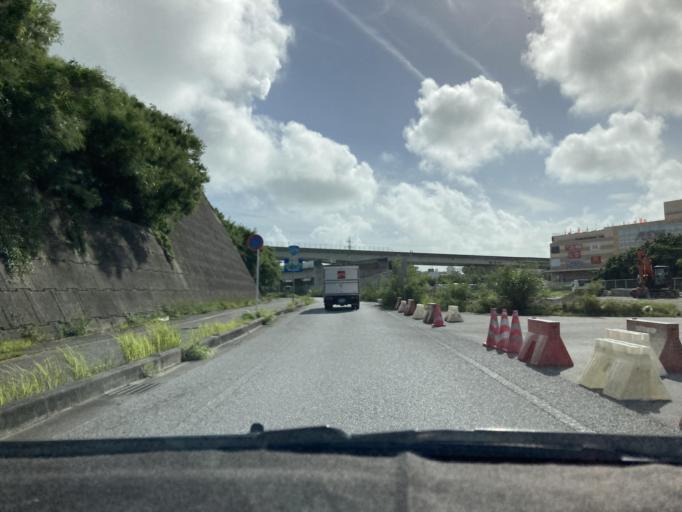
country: JP
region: Okinawa
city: Naha-shi
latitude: 26.2025
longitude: 127.7370
